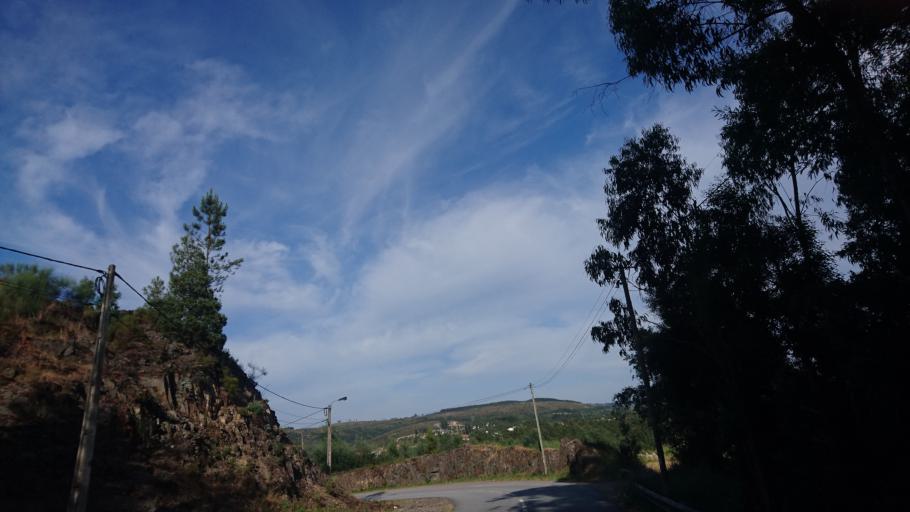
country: PT
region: Porto
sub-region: Paredes
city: Recarei
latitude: 41.1298
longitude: -8.4275
